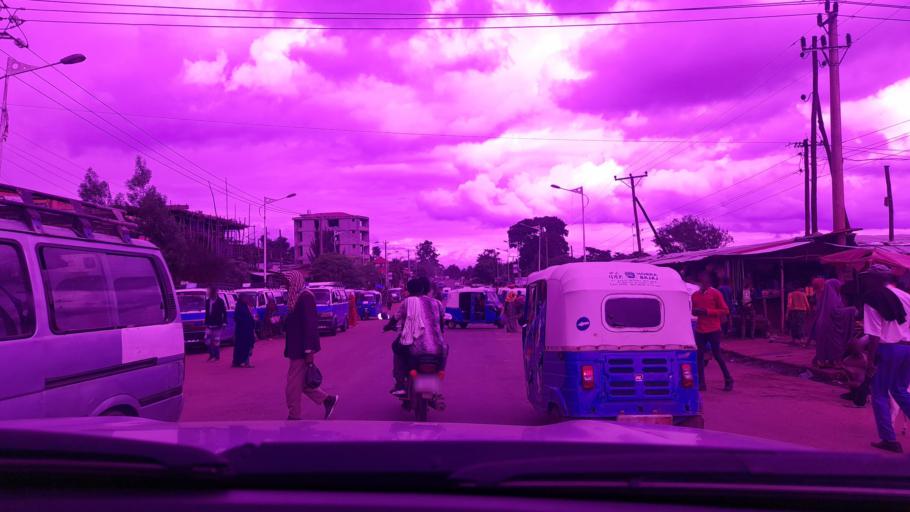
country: ET
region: Oromiya
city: Jima
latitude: 7.6729
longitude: 36.8545
